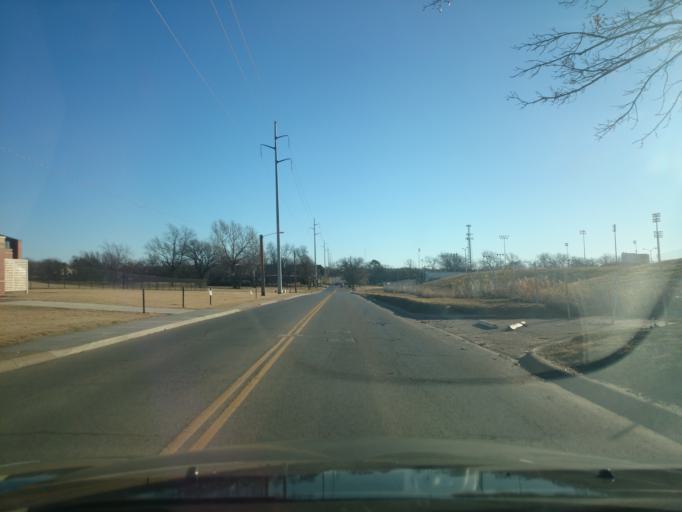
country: US
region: Oklahoma
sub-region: Payne County
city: Stillwater
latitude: 36.1305
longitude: -97.0664
